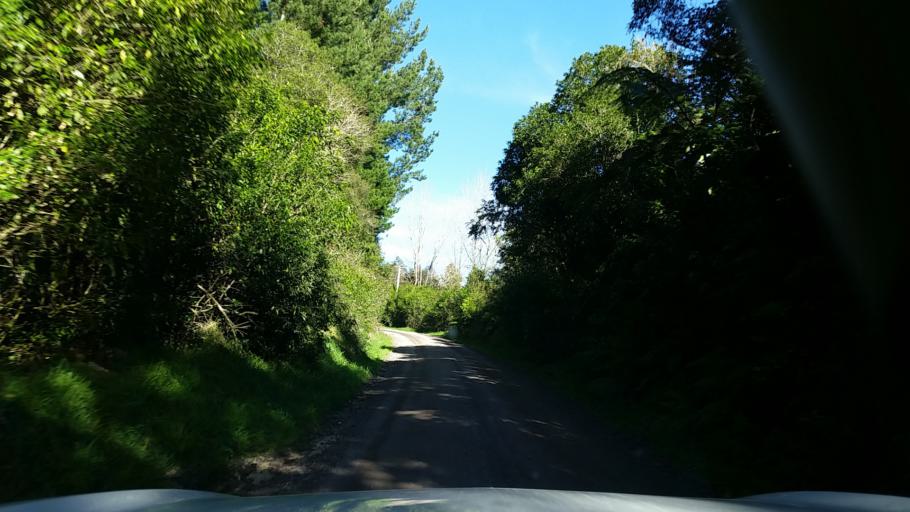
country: NZ
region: Waikato
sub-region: Taupo District
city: Taupo
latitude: -38.4042
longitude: 176.1407
